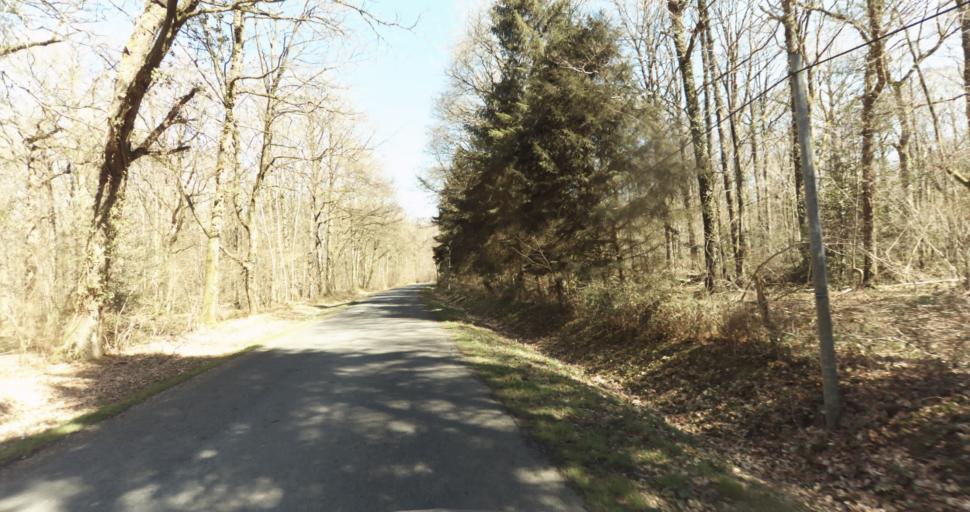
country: FR
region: Lower Normandy
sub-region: Departement de l'Orne
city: Trun
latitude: 48.9307
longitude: 0.0697
